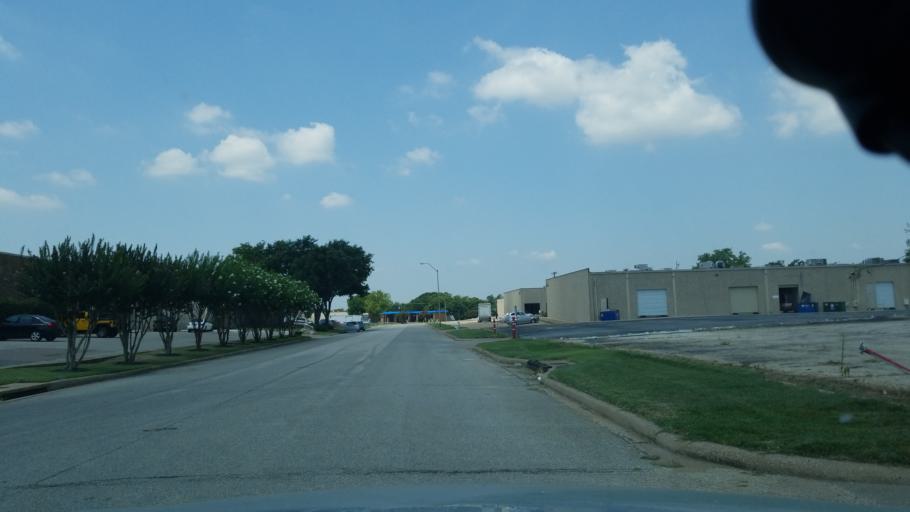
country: US
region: Texas
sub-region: Dallas County
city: Carrollton
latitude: 32.9516
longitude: -96.8673
